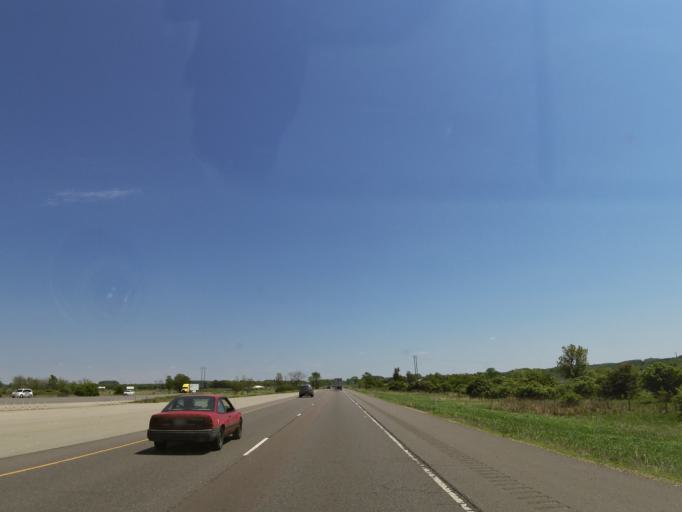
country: US
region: Wisconsin
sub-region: Monroe County
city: Tomah
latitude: 43.9594
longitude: -90.3674
